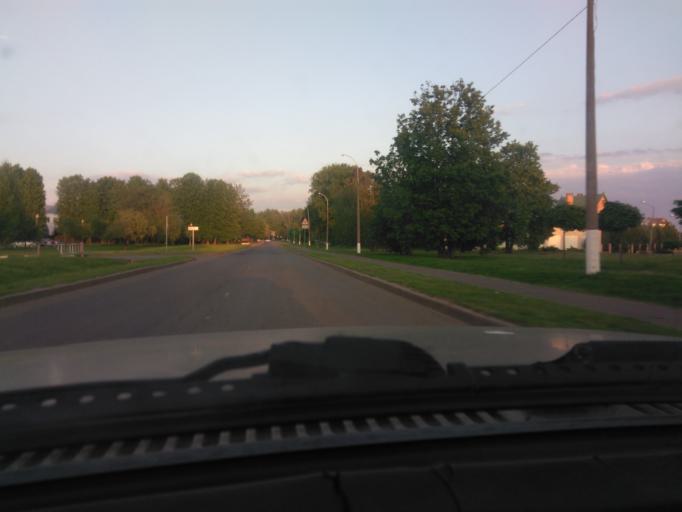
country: BY
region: Mogilev
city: Mahilyow
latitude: 53.9293
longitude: 30.3079
